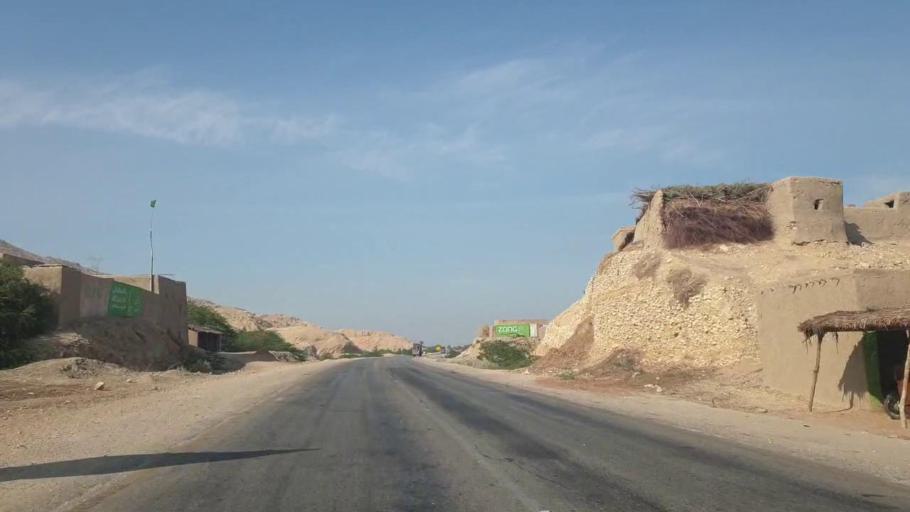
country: PK
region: Sindh
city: Sehwan
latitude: 26.3043
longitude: 67.8936
